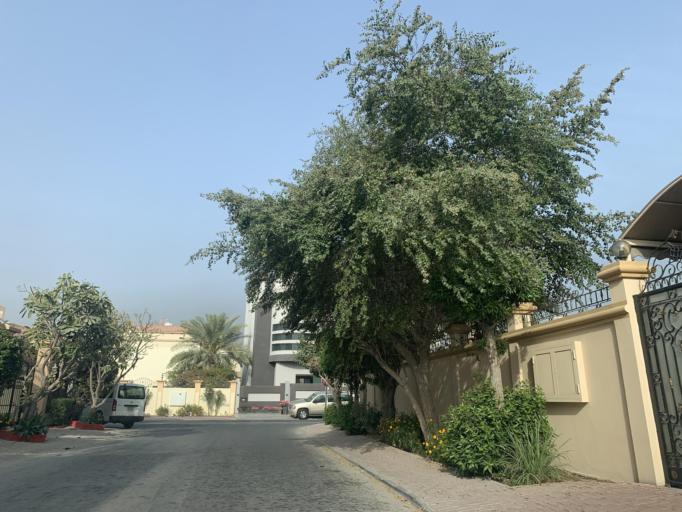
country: BH
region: Northern
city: Madinat `Isa
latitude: 26.1921
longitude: 50.5612
